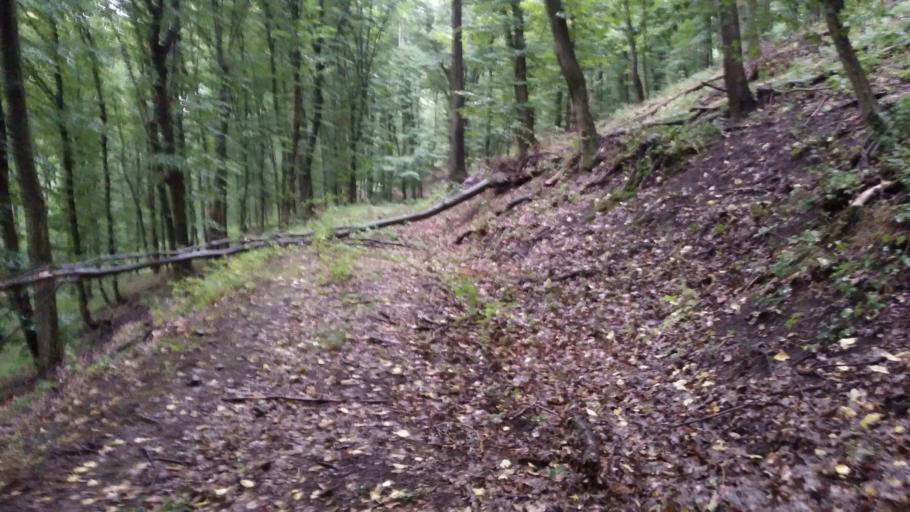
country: HU
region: Pest
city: Szob
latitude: 47.9160
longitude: 18.8761
